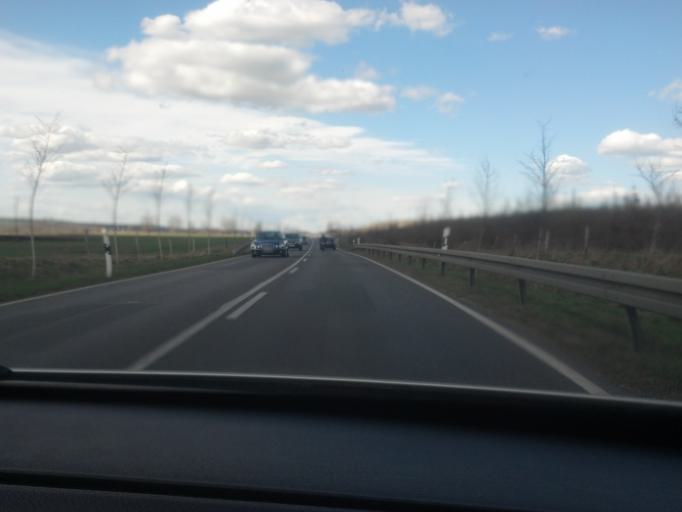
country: DE
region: Mecklenburg-Vorpommern
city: Trollenhagen
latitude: 53.6068
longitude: 13.2680
